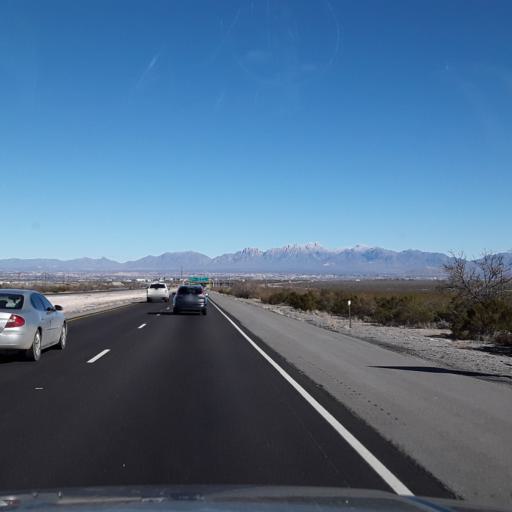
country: US
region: New Mexico
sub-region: Dona Ana County
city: Mesilla
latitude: 32.2781
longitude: -106.8950
